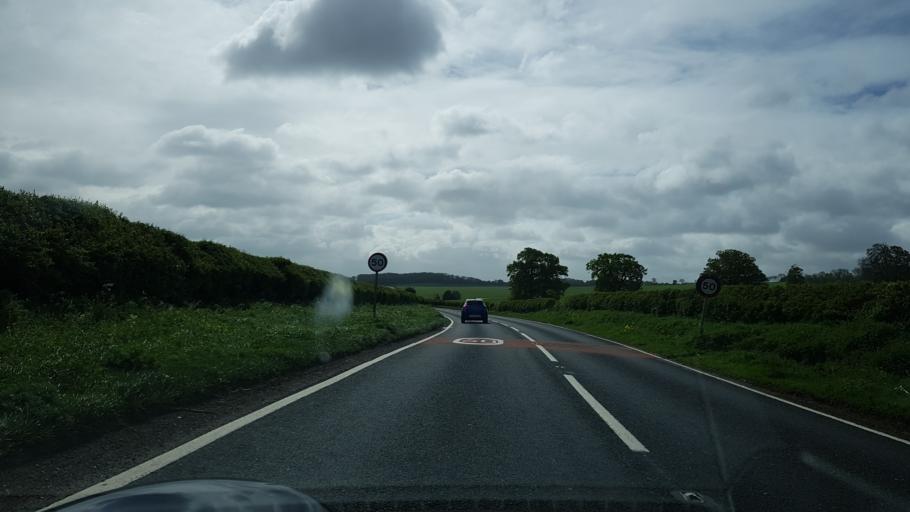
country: GB
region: England
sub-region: Hampshire
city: Kingsclere
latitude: 51.3054
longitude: -1.1927
